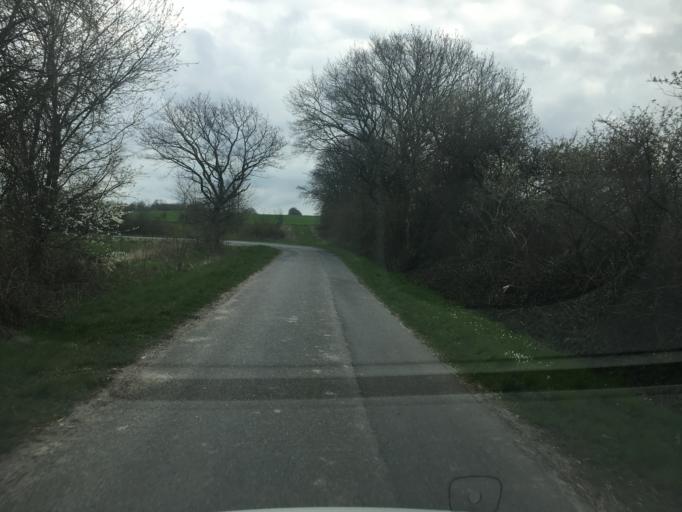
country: DE
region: Schleswig-Holstein
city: Glucksburg
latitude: 54.9006
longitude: 9.5130
